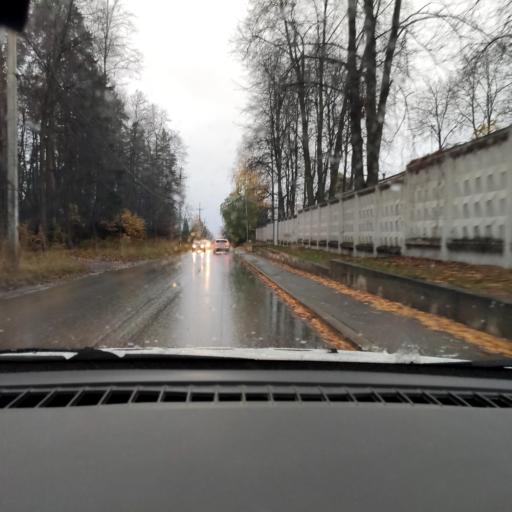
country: RU
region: Perm
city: Kondratovo
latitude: 58.0524
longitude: 56.1218
